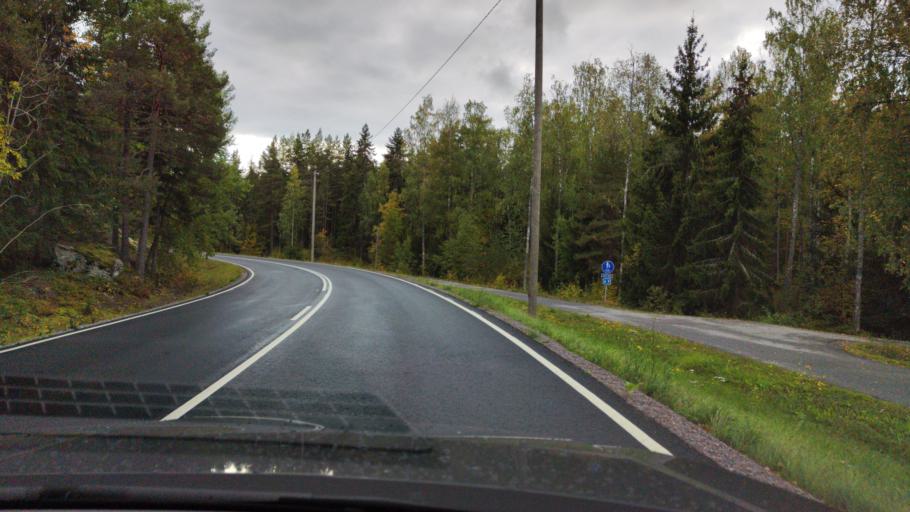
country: FI
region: Varsinais-Suomi
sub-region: Turku
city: Raisio
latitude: 60.3715
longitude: 22.1762
